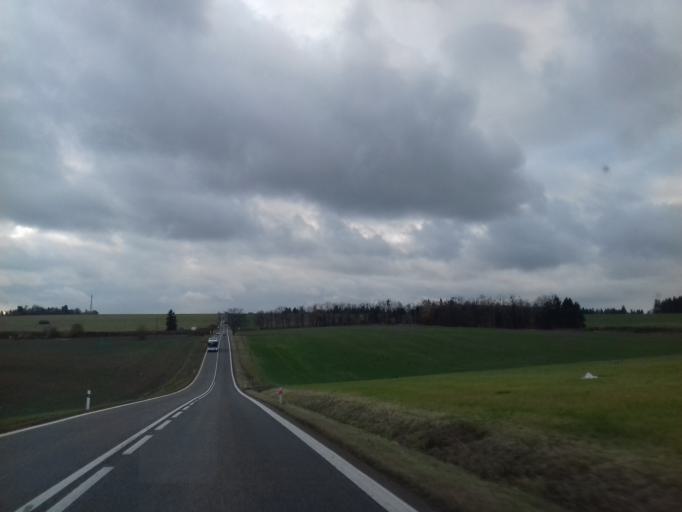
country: CZ
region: Pardubicky
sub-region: Okres Svitavy
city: Svitavy
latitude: 49.7477
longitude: 16.4197
